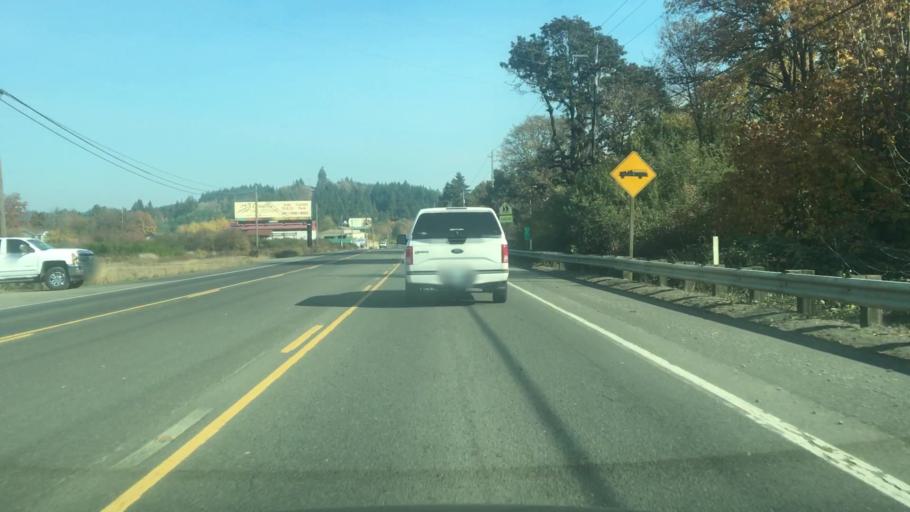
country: US
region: Oregon
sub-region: Polk County
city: Grand Ronde
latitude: 45.0585
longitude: -123.6139
